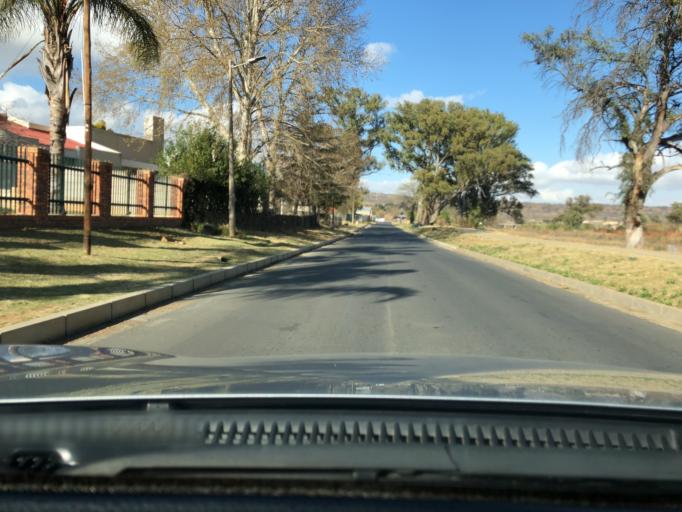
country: ZA
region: KwaZulu-Natal
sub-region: uThukela District Municipality
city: Ladysmith
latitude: -28.5623
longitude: 29.7773
